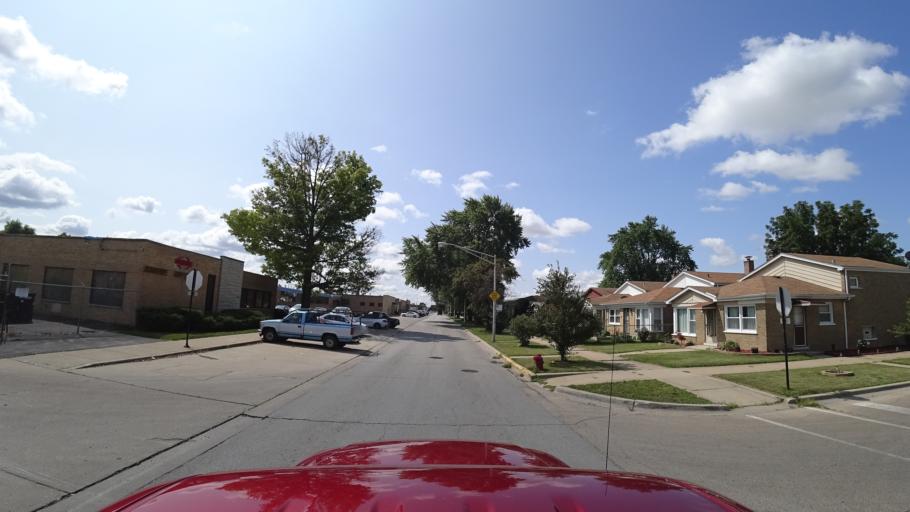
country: US
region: Illinois
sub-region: Cook County
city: Cicero
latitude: 41.8114
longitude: -87.7396
